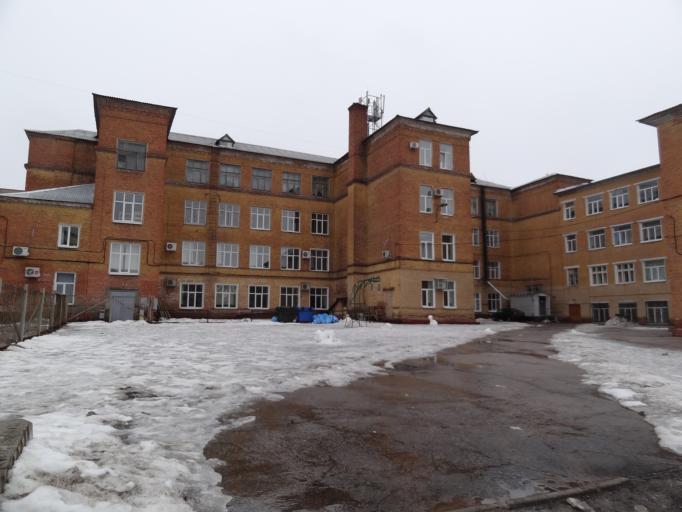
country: RU
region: Saratov
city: Engel's
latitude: 51.4960
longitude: 46.1164
